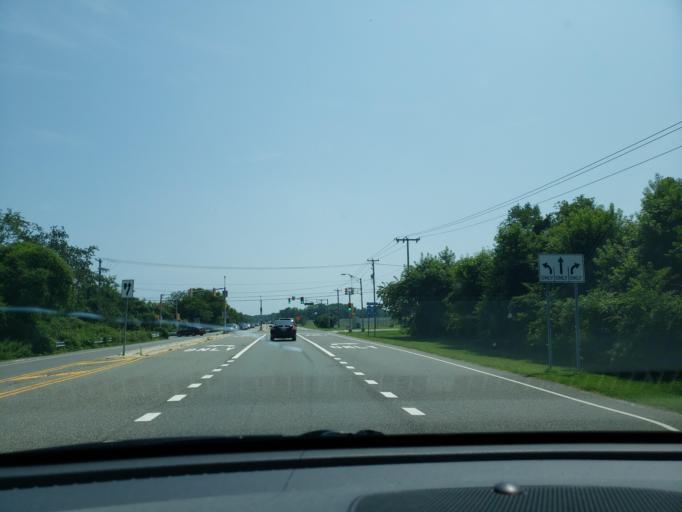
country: US
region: New Jersey
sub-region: Cape May County
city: Erma
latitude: 38.9719
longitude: -74.9285
